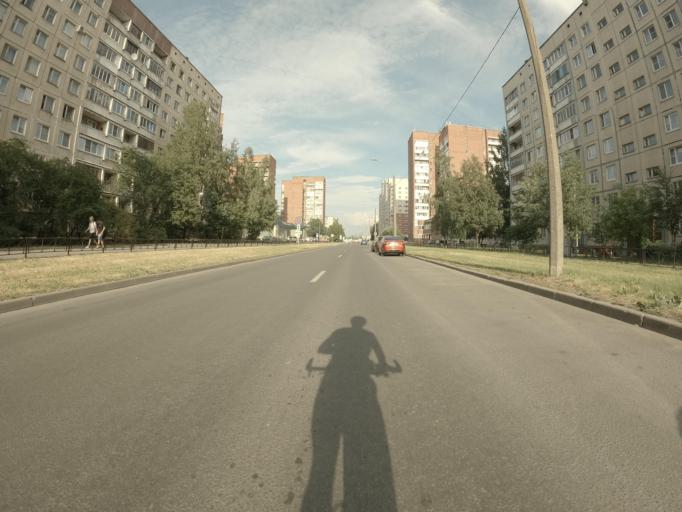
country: RU
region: St.-Petersburg
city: Krasnogvargeisky
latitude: 59.9403
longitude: 30.4919
